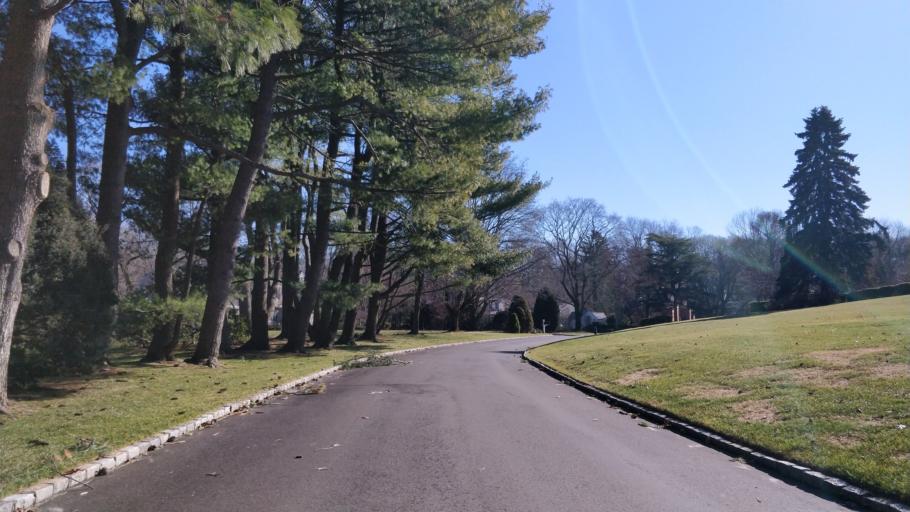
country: US
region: New York
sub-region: Nassau County
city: Brookville
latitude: 40.8145
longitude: -73.5726
